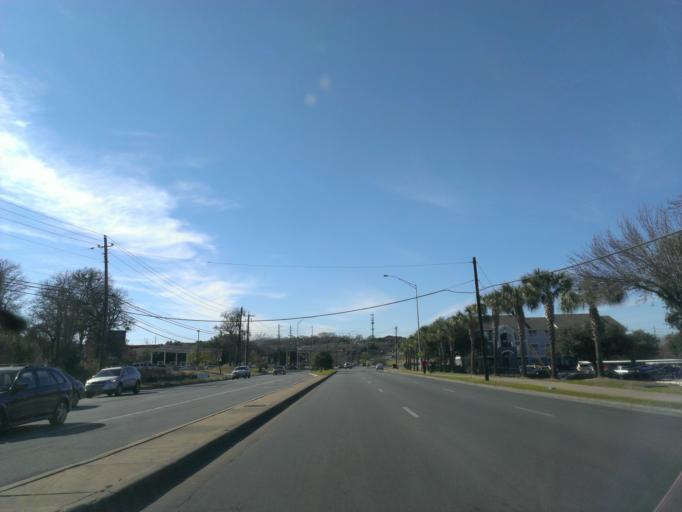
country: US
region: Texas
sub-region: Travis County
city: Austin
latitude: 30.2320
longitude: -97.7185
